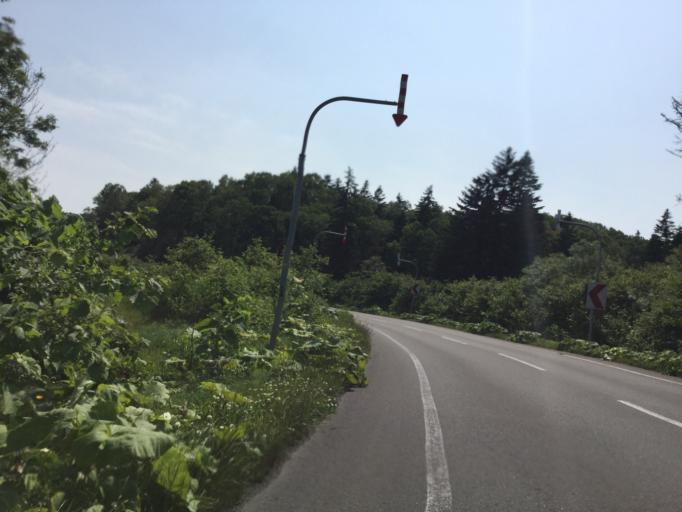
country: JP
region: Hokkaido
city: Makubetsu
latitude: 45.4109
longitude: 141.9996
